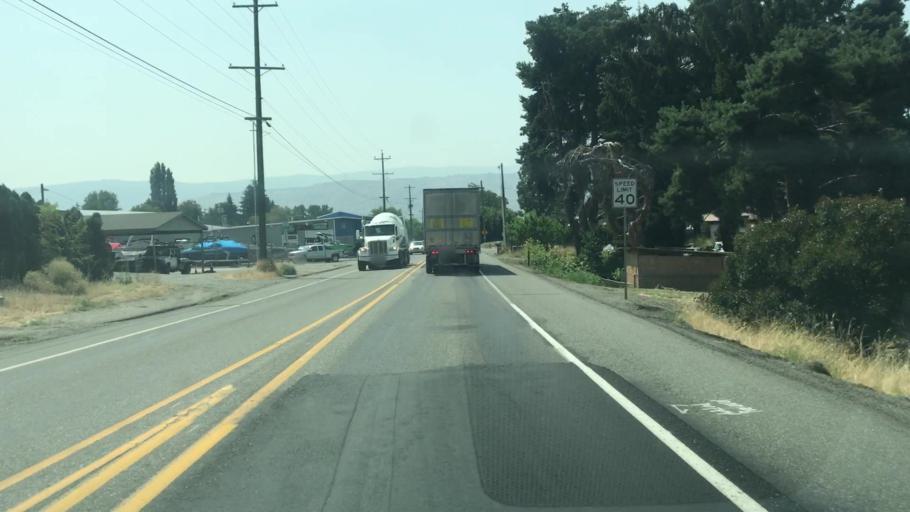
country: US
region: Washington
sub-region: Chelan County
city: Wenatchee
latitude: 47.4413
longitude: -120.2975
